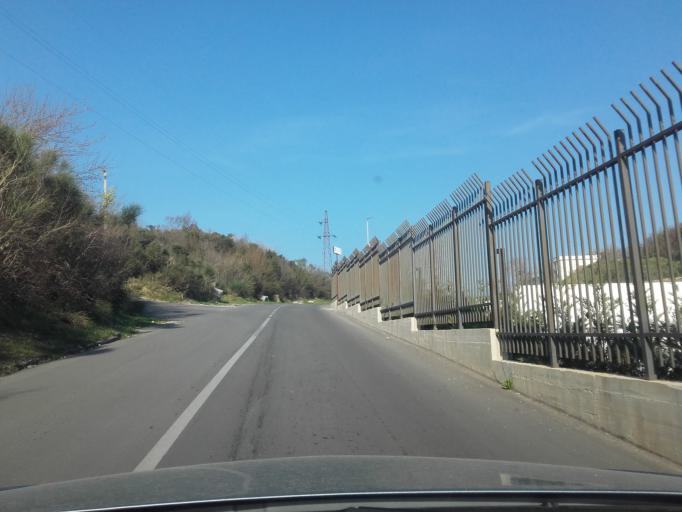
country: ME
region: Budva
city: Budva
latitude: 42.2928
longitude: 18.8205
